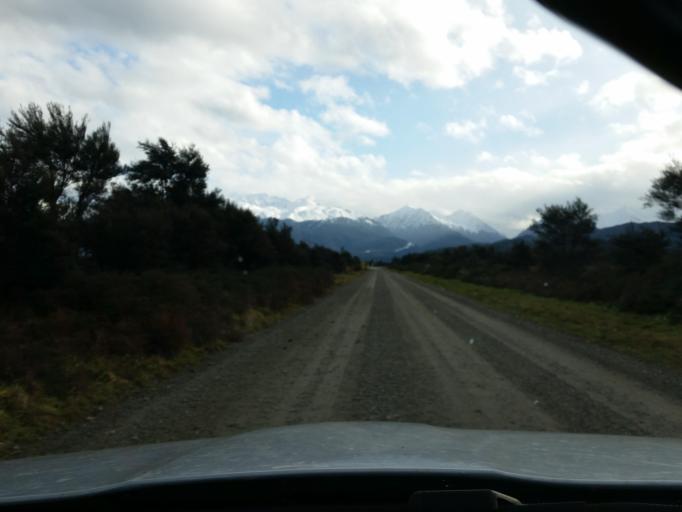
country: NZ
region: Southland
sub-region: Southland District
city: Te Anau
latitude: -45.7816
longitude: 167.6056
